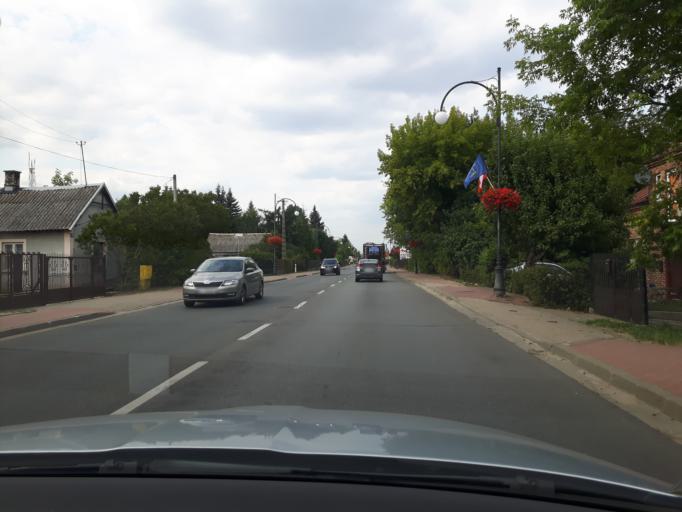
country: PL
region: Masovian Voivodeship
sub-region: Powiat legionowski
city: Nieporet
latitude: 52.4228
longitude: 21.0348
